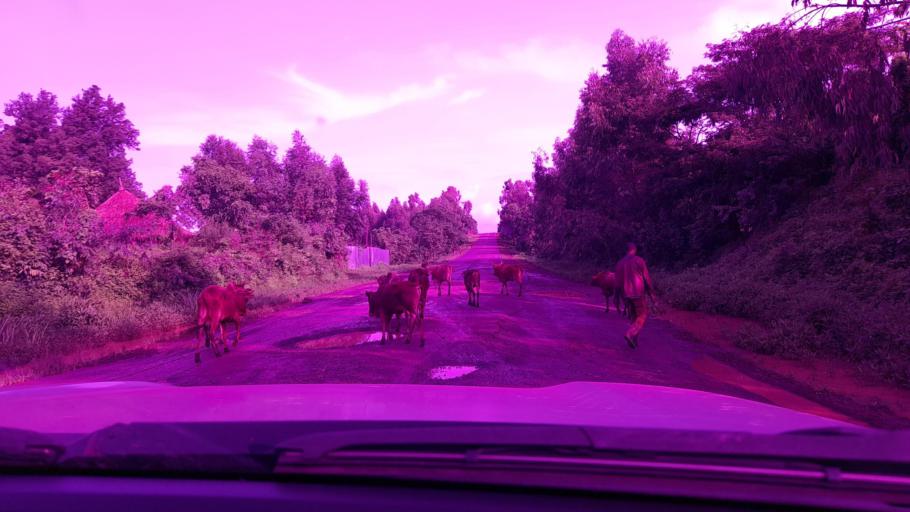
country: ET
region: Oromiya
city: Bedele
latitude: 8.1859
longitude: 36.4498
